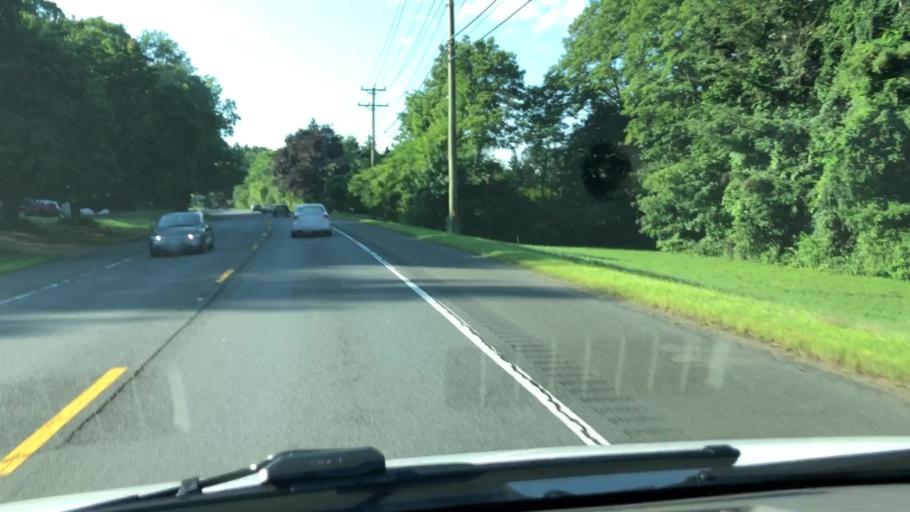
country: US
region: Massachusetts
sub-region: Hampshire County
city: North Amherst
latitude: 42.4445
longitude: -72.5535
